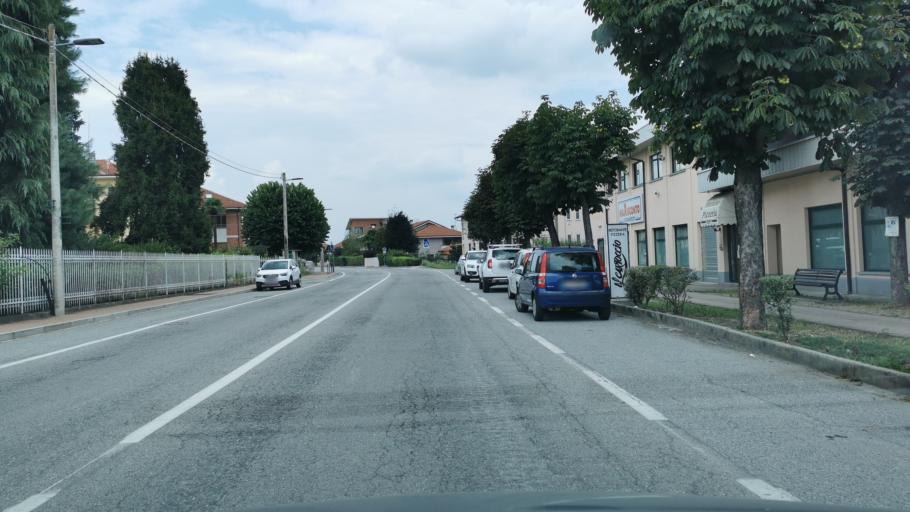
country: IT
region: Piedmont
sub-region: Provincia di Torino
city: Cavour
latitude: 44.7881
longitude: 7.3755
